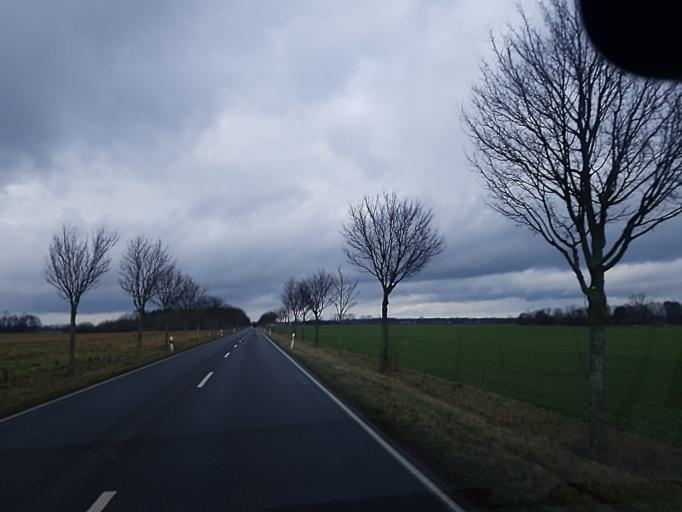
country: DE
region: Brandenburg
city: Bad Liebenwerda
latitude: 51.4936
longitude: 13.3902
